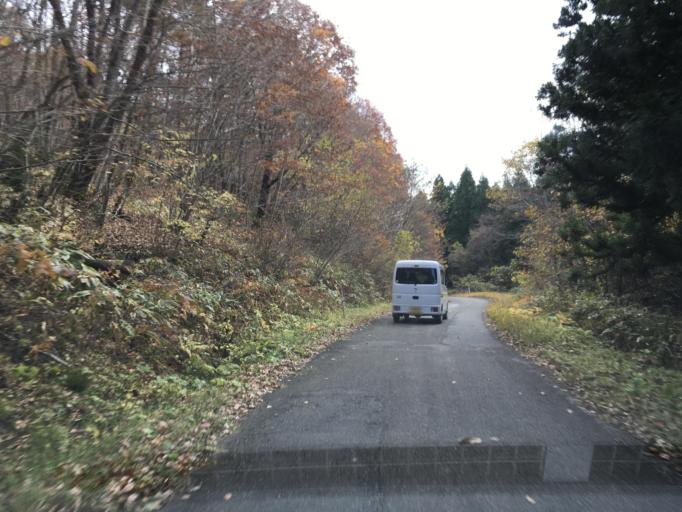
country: JP
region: Iwate
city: Mizusawa
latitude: 39.1260
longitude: 141.3179
